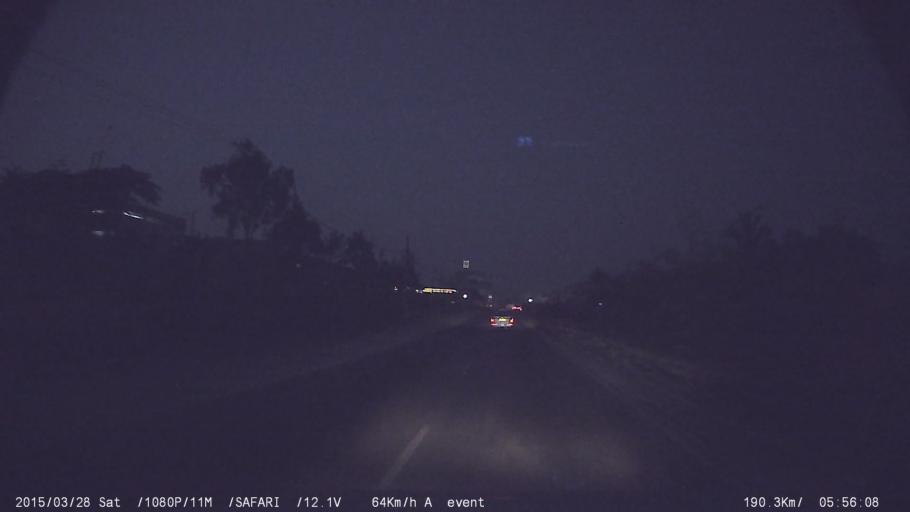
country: IN
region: Karnataka
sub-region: Bangalore Urban
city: Bangalore
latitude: 12.8959
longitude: 77.4605
